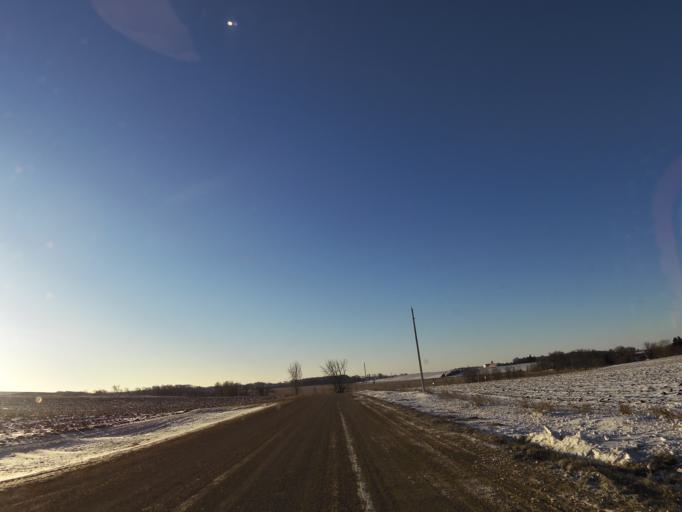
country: US
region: Minnesota
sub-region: Scott County
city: Jordan
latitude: 44.6659
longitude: -93.5419
